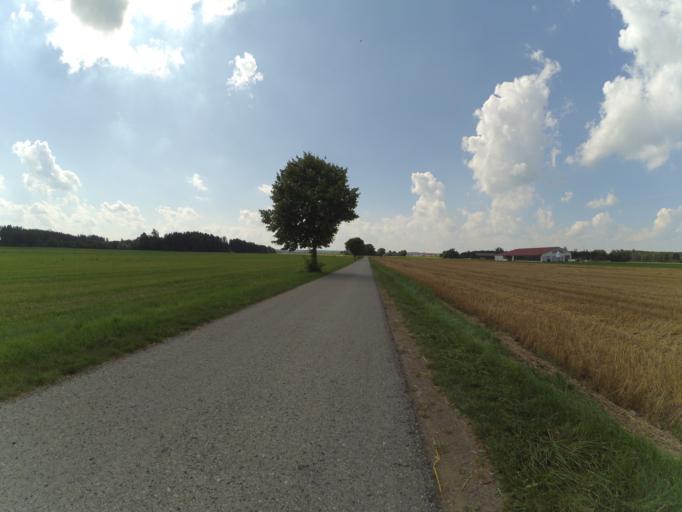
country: DE
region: Bavaria
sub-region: Swabia
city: Bad Worishofen
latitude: 48.0010
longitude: 10.6293
